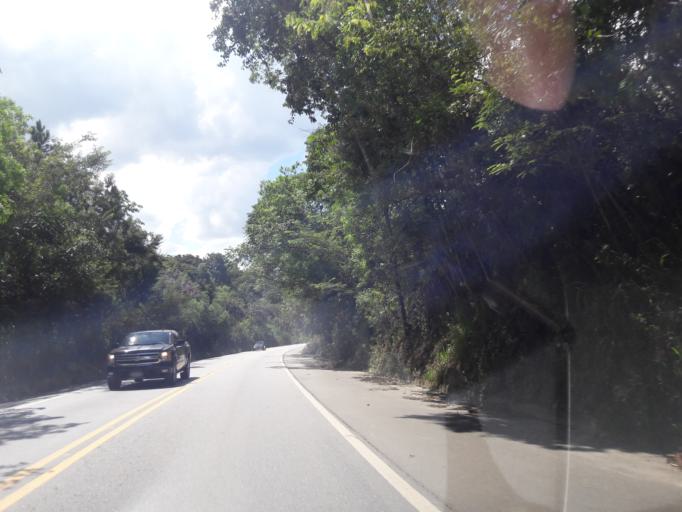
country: BR
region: Sao Paulo
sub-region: Campo Limpo Paulista
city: Campo Limpo Paulista
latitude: -23.2436
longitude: -46.7921
